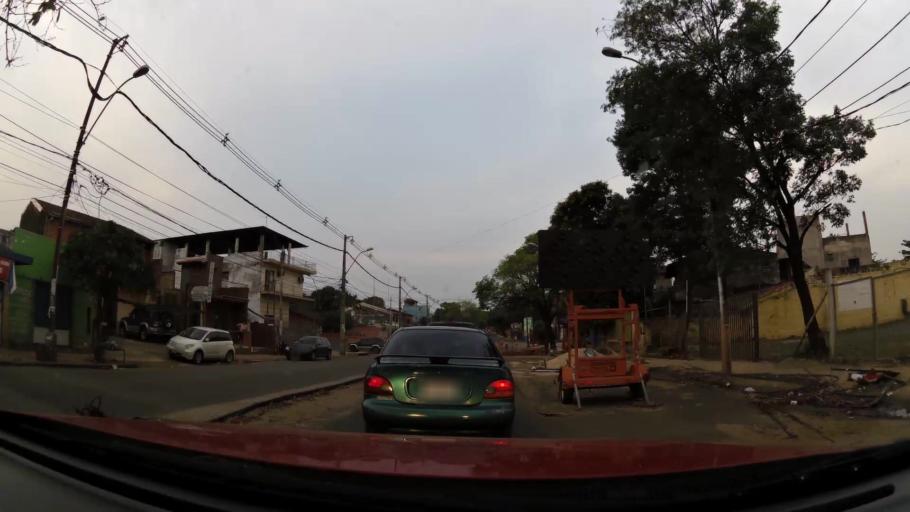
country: PY
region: Asuncion
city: Asuncion
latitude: -25.3118
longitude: -57.6172
